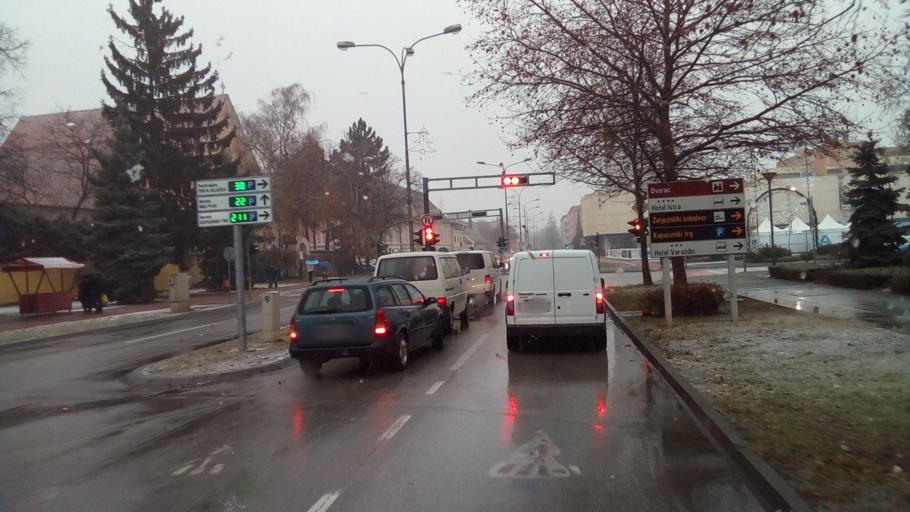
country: HR
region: Varazdinska
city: Varazdin
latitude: 46.3044
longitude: 16.3348
